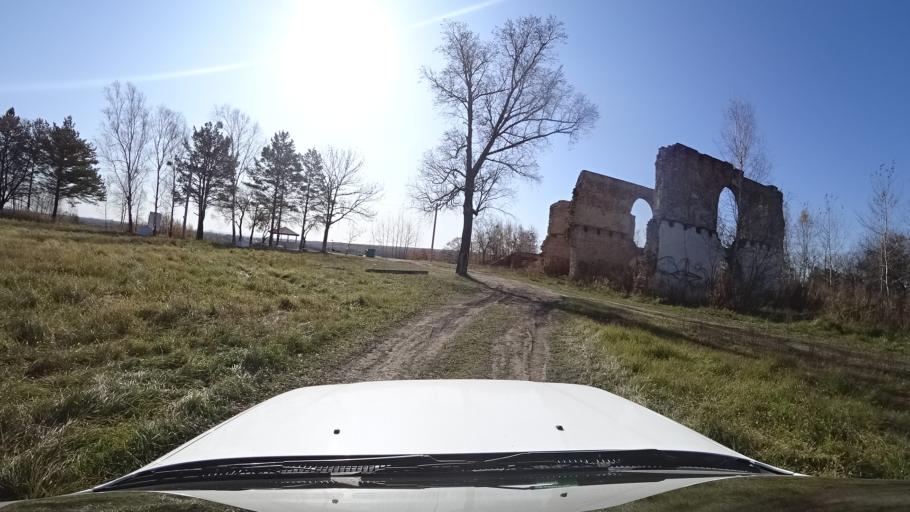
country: RU
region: Primorskiy
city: Dal'nerechensk
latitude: 45.9461
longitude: 133.6863
